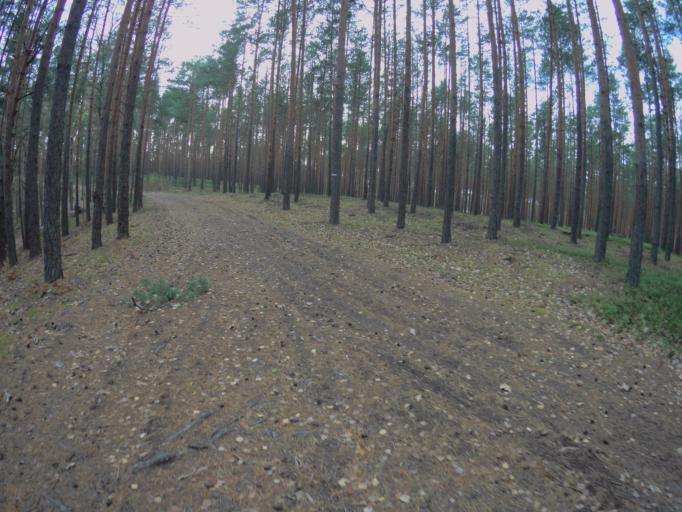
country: PL
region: Subcarpathian Voivodeship
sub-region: Powiat kolbuszowski
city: Lipnica
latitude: 50.3312
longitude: 21.9356
